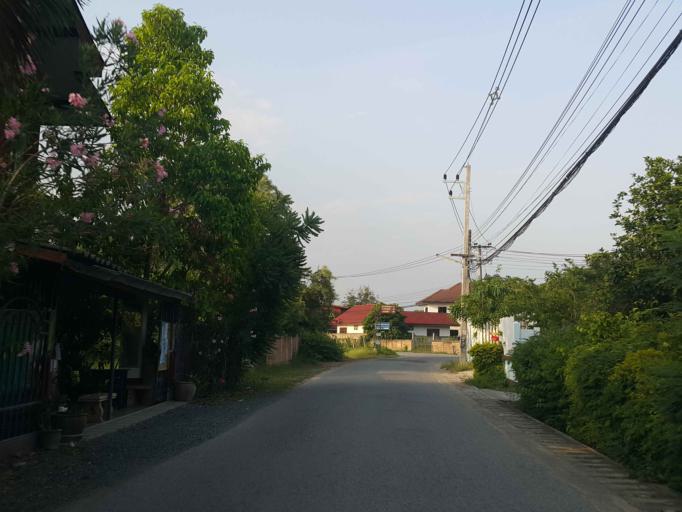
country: TH
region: Chiang Mai
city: San Sai
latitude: 18.8037
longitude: 99.0911
